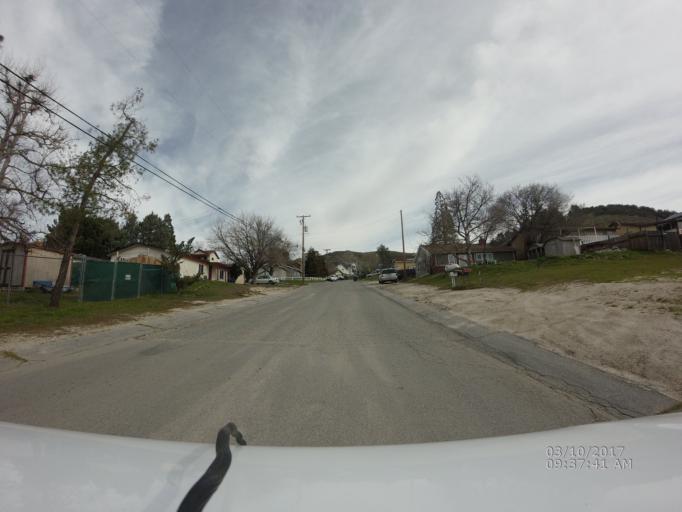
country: US
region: California
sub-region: Los Angeles County
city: Green Valley
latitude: 34.6663
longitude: -118.3897
